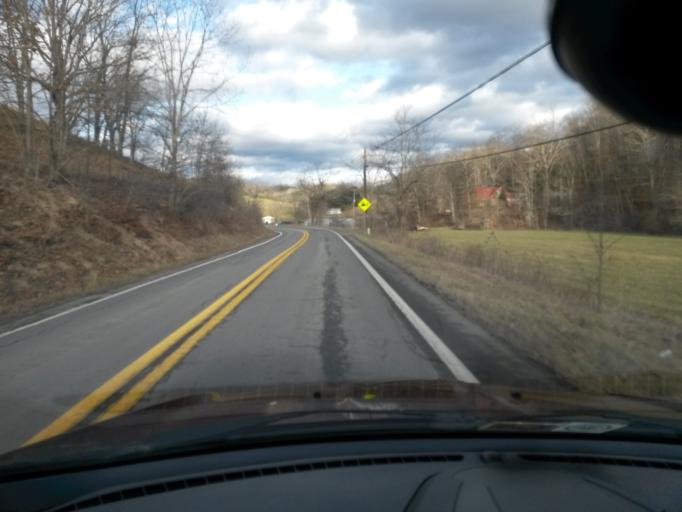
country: US
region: Virginia
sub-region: Giles County
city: Pembroke
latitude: 37.4683
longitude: -80.6588
